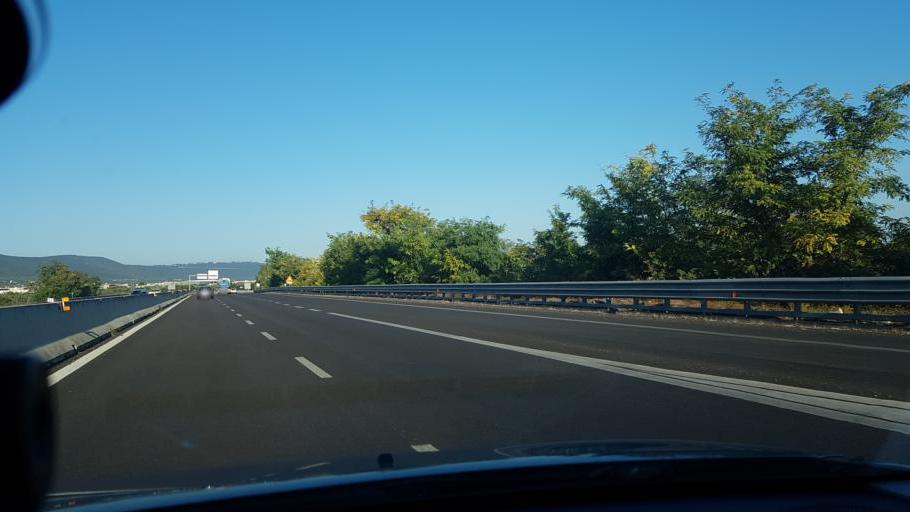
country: IT
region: Apulia
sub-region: Provincia di Brindisi
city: Fasano
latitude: 40.8411
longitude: 17.3705
